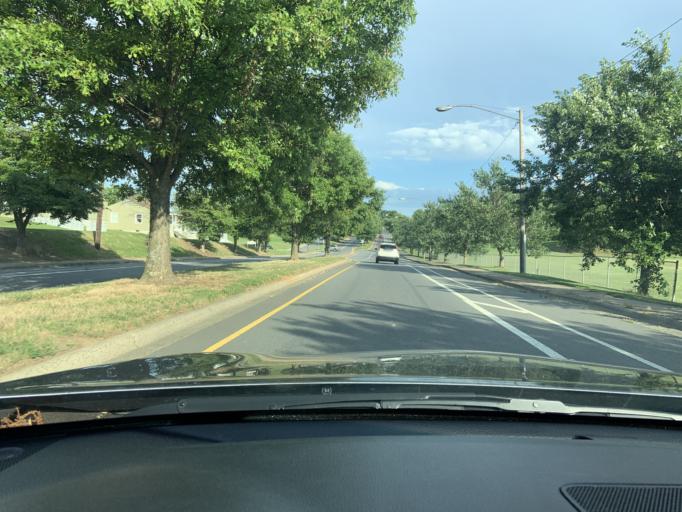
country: US
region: North Carolina
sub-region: Mecklenburg County
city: Charlotte
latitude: 35.2084
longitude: -80.8729
